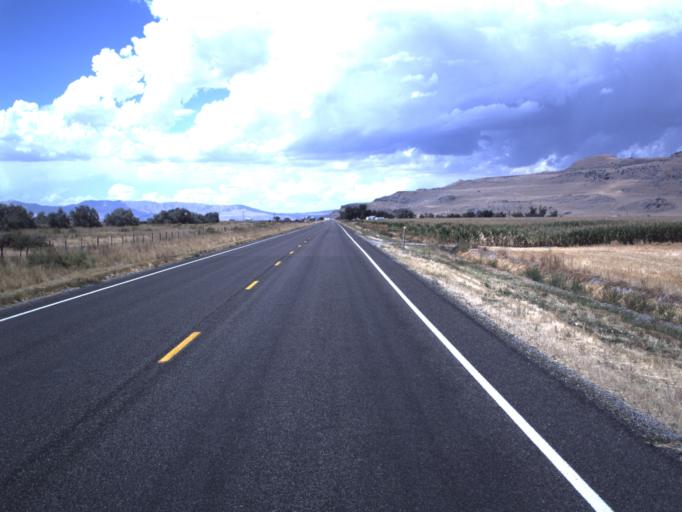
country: US
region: Utah
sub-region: Box Elder County
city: Honeyville
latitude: 41.5671
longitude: -112.1869
